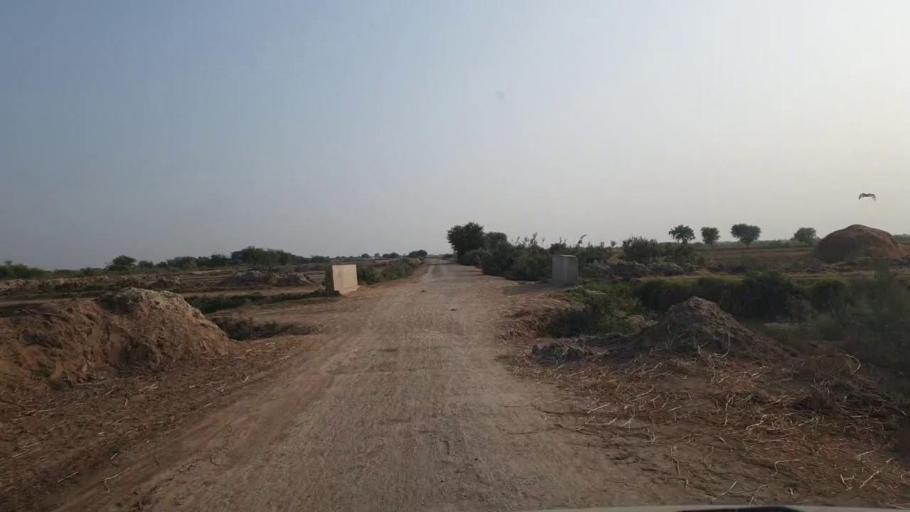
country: PK
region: Sindh
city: Matli
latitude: 25.0561
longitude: 68.7628
